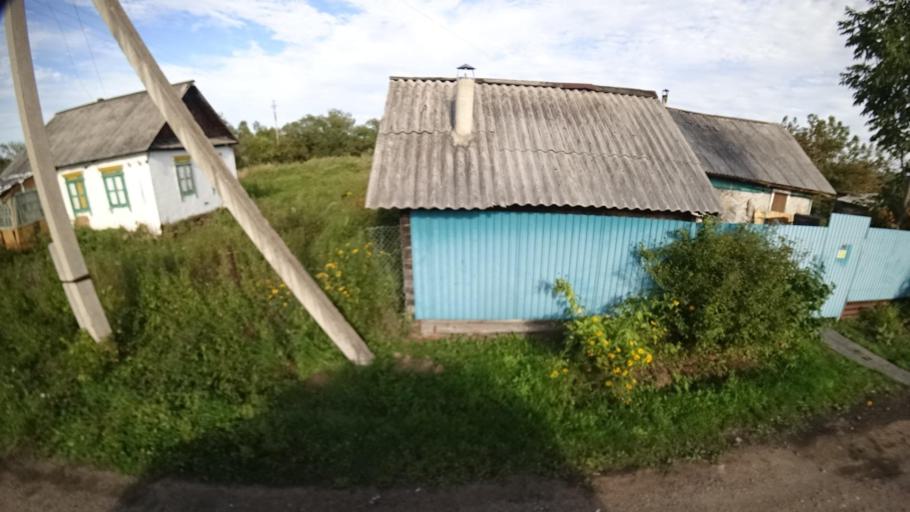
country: RU
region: Primorskiy
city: Dostoyevka
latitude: 44.2918
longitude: 133.4301
